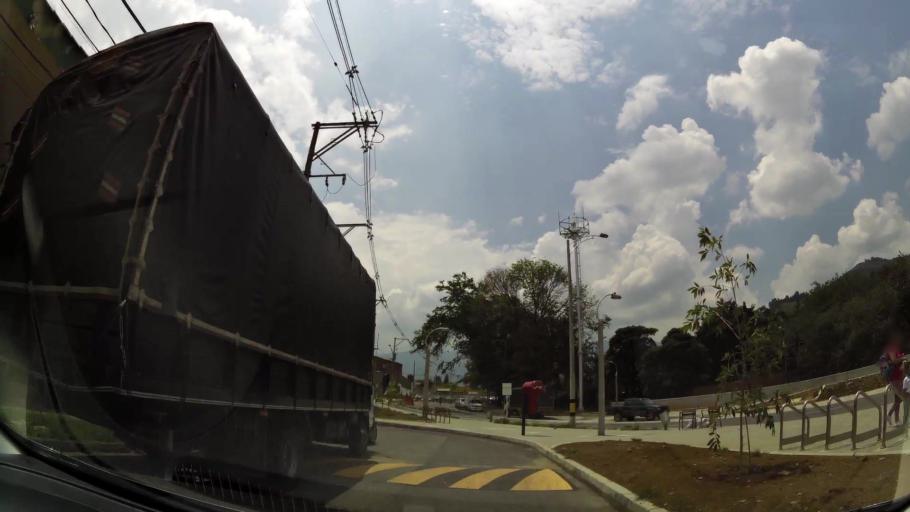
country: CO
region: Antioquia
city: Itagui
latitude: 6.1739
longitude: -75.6093
